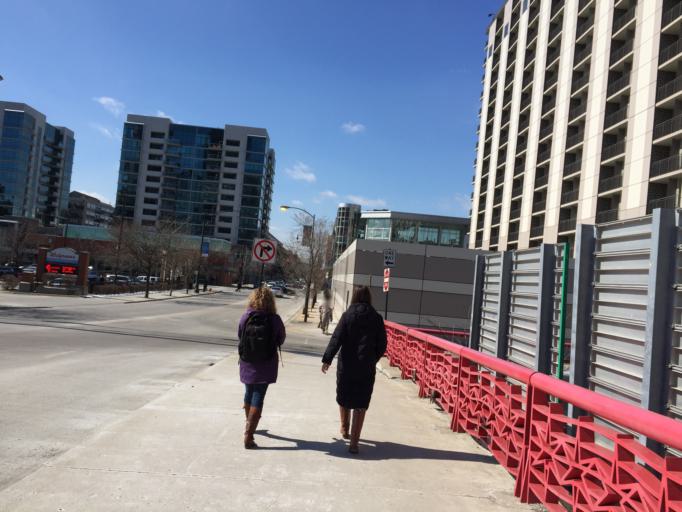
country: US
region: Illinois
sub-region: Cook County
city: Chicago
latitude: 41.8806
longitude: -87.6461
